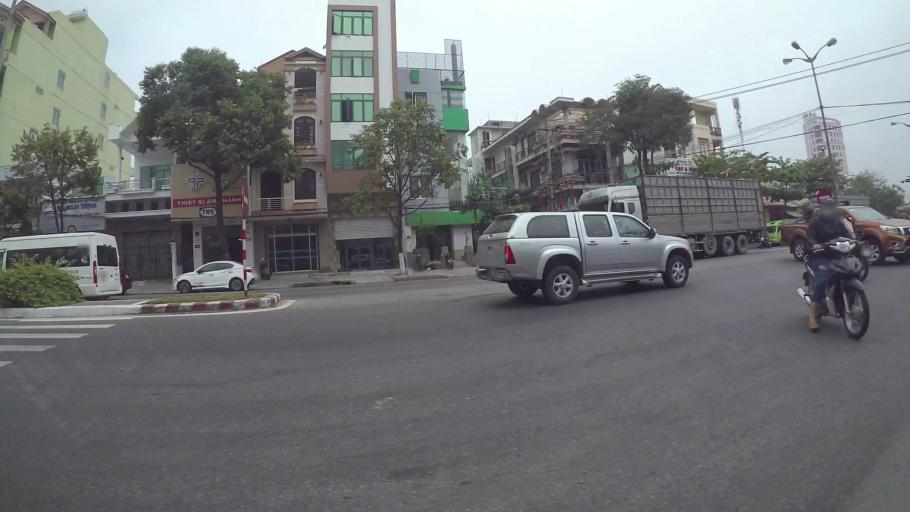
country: VN
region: Da Nang
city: Cam Le
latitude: 16.0310
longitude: 108.2239
